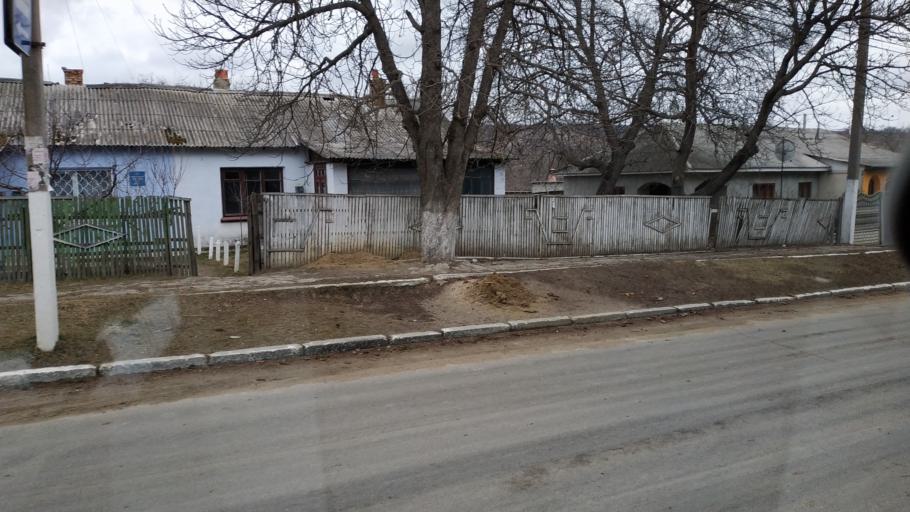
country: MD
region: Calarasi
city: Calarasi
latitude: 47.2049
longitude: 28.2450
